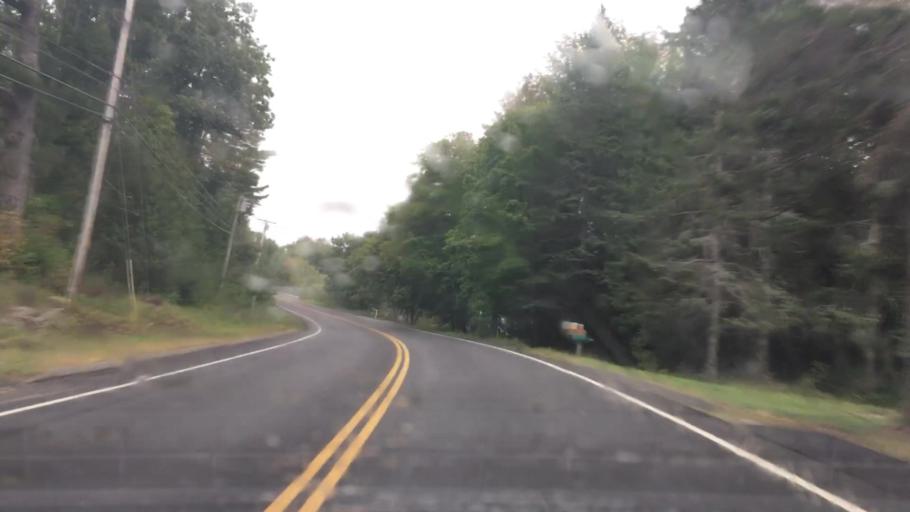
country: US
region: Maine
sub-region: Penobscot County
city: Orrington
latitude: 44.6836
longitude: -68.8103
